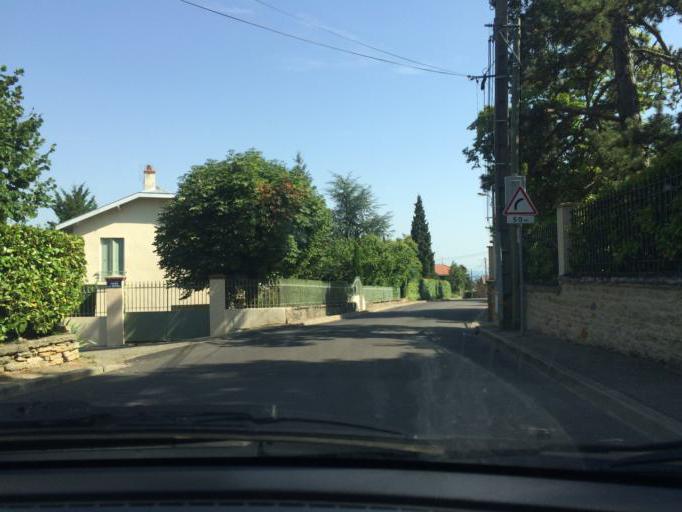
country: FR
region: Rhone-Alpes
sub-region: Departement du Rhone
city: Limonest
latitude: 45.8214
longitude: 4.7954
